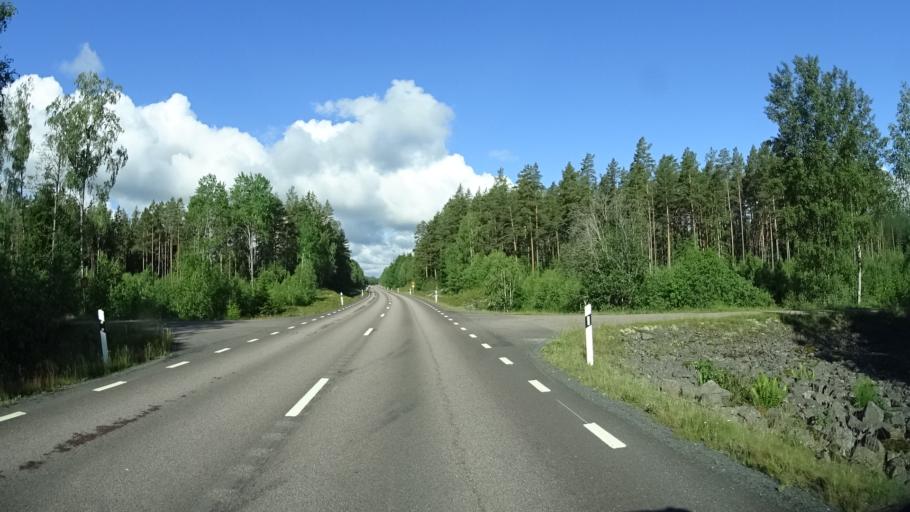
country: SE
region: Kalmar
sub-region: Hogsby Kommun
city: Hoegsby
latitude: 57.1365
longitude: 15.8043
